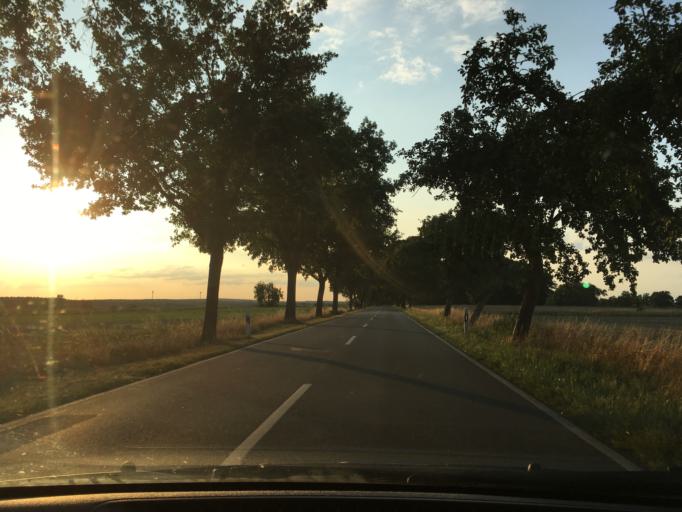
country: DE
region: Lower Saxony
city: Dahlem
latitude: 53.2467
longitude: 10.7773
